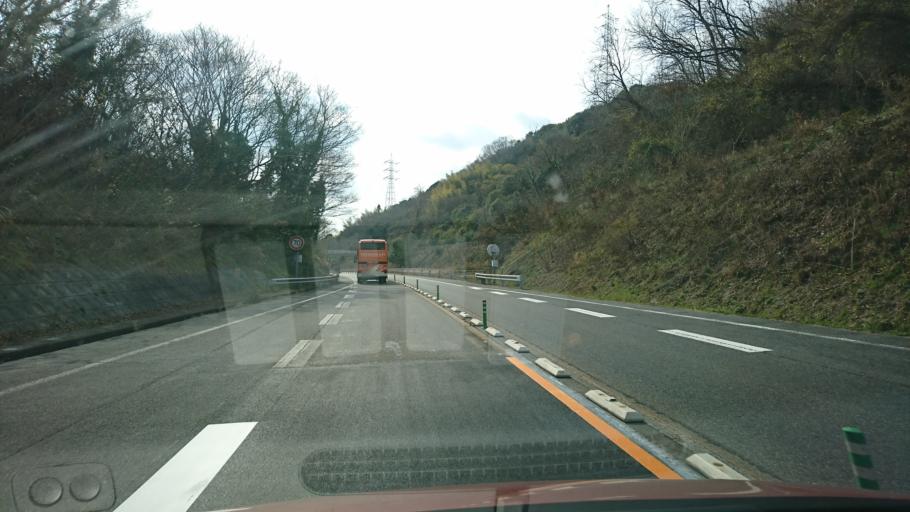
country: JP
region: Hiroshima
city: Innoshima
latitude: 34.2271
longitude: 133.0465
